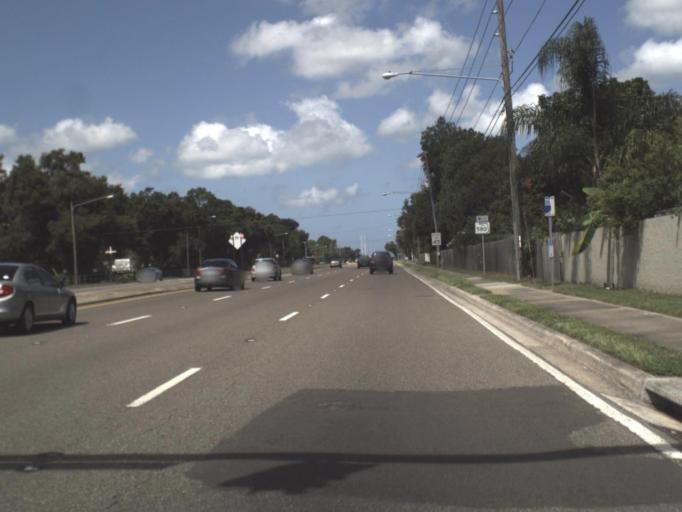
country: US
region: Florida
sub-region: Pinellas County
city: Safety Harbor
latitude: 28.0197
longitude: -82.7166
